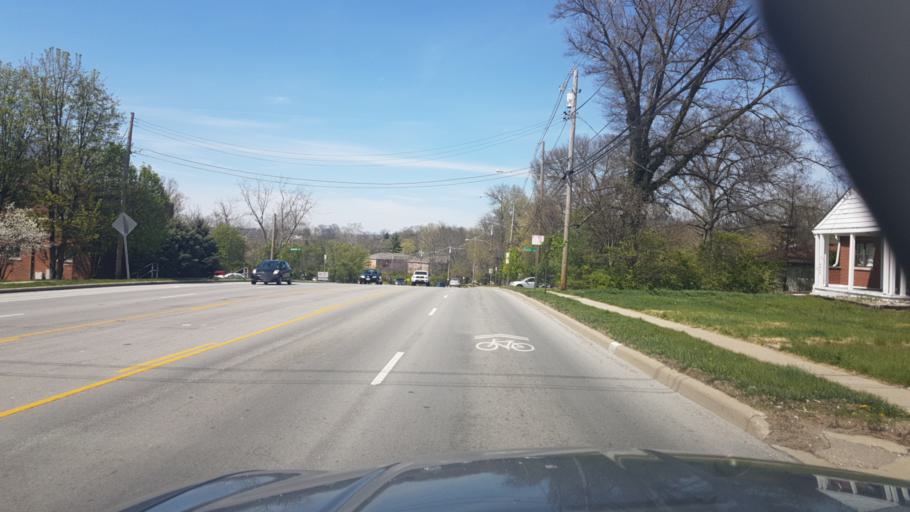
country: US
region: Ohio
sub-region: Hamilton County
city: Turpin Hills
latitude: 39.1021
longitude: -84.3870
